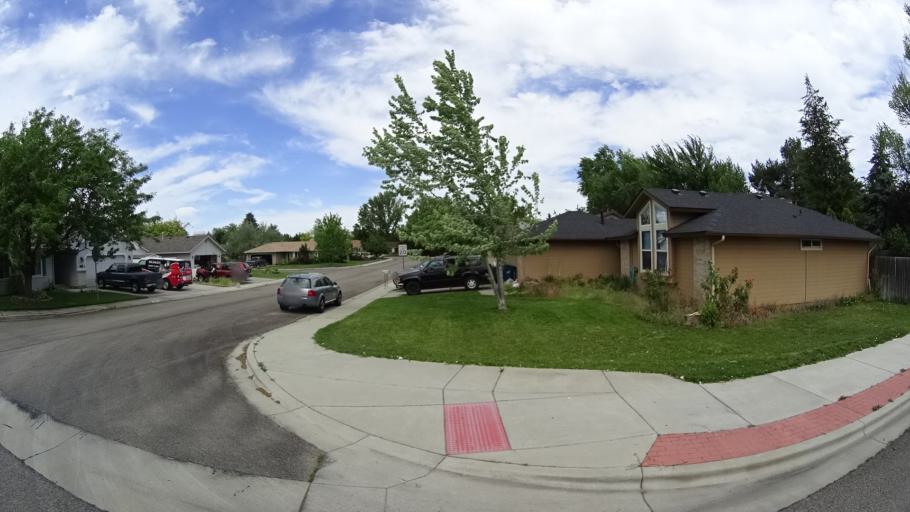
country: US
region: Idaho
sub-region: Ada County
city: Garden City
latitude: 43.6340
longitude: -116.2919
